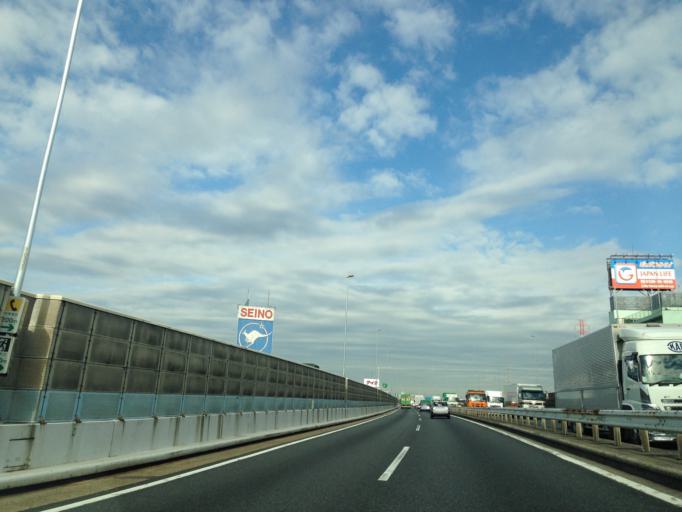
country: JP
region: Saitama
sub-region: Kawaguchi-shi
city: Hatogaya-honcho
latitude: 35.7984
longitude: 139.7615
